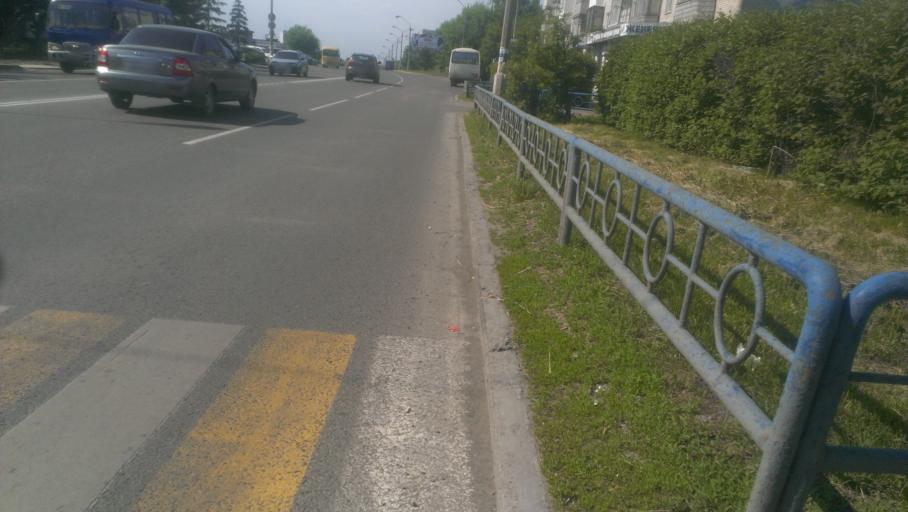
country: RU
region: Altai Krai
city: Novoaltaysk
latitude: 53.3934
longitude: 83.9336
